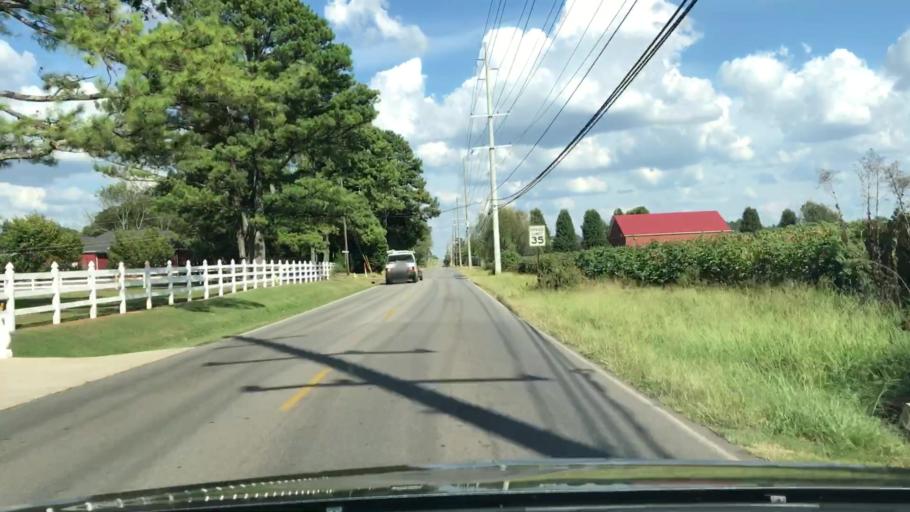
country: US
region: Alabama
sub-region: Madison County
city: Harvest
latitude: 34.8084
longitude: -86.7462
